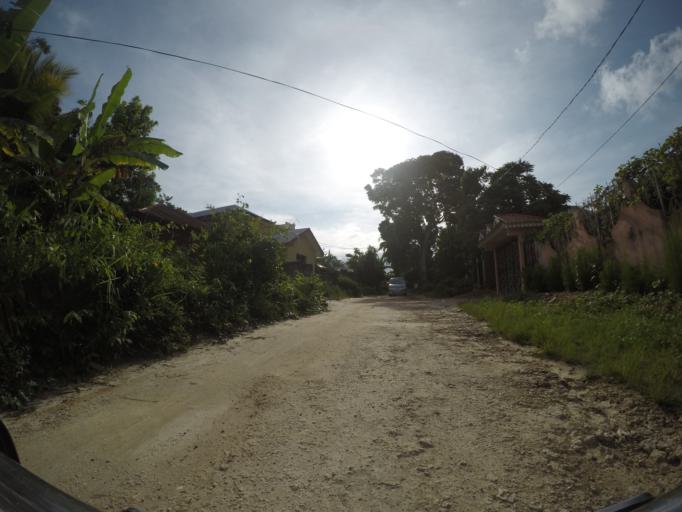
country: TZ
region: Pemba South
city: Chake Chake
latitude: -5.2263
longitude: 39.7768
